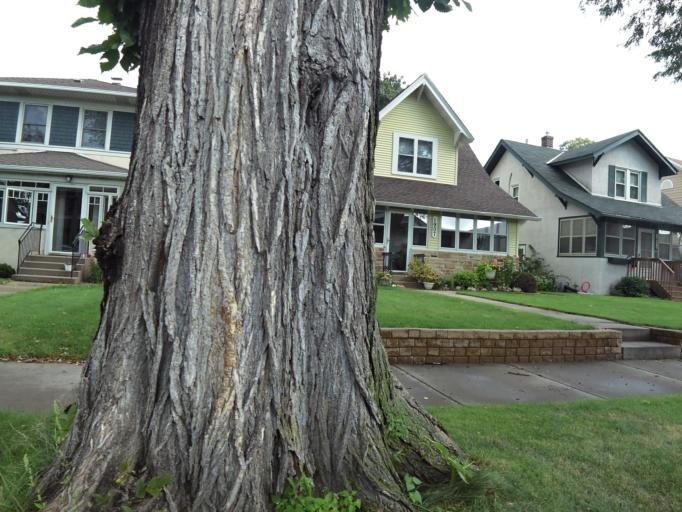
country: US
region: Minnesota
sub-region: Ramsey County
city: Falcon Heights
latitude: 44.9325
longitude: -93.1810
